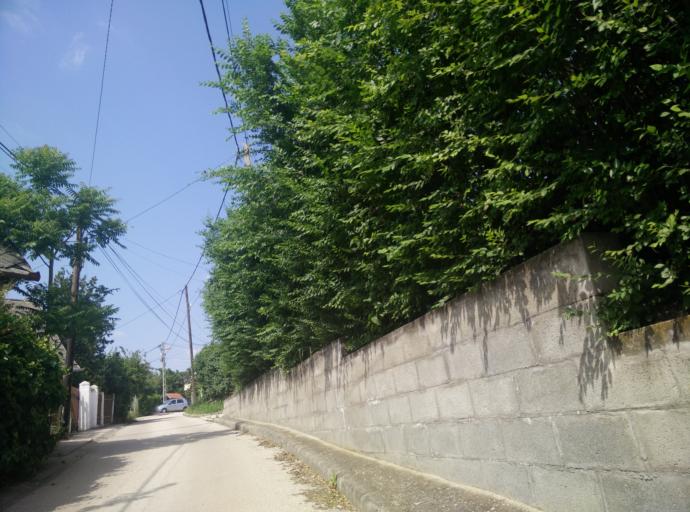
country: HU
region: Pest
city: Biatorbagy
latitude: 47.4638
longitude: 18.8042
